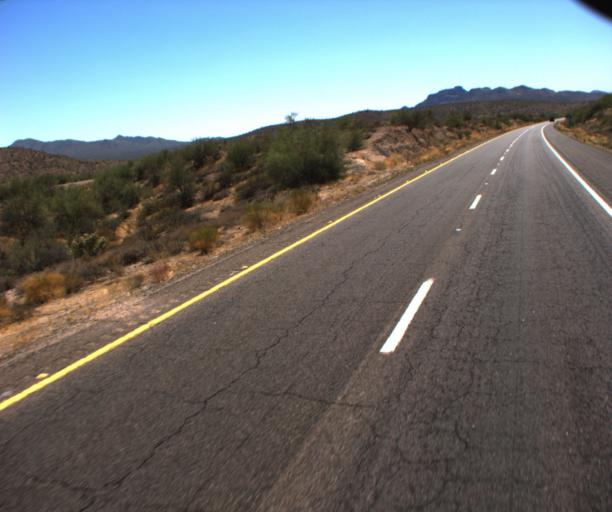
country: US
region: Arizona
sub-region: Maricopa County
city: Fountain Hills
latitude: 33.5863
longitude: -111.6067
